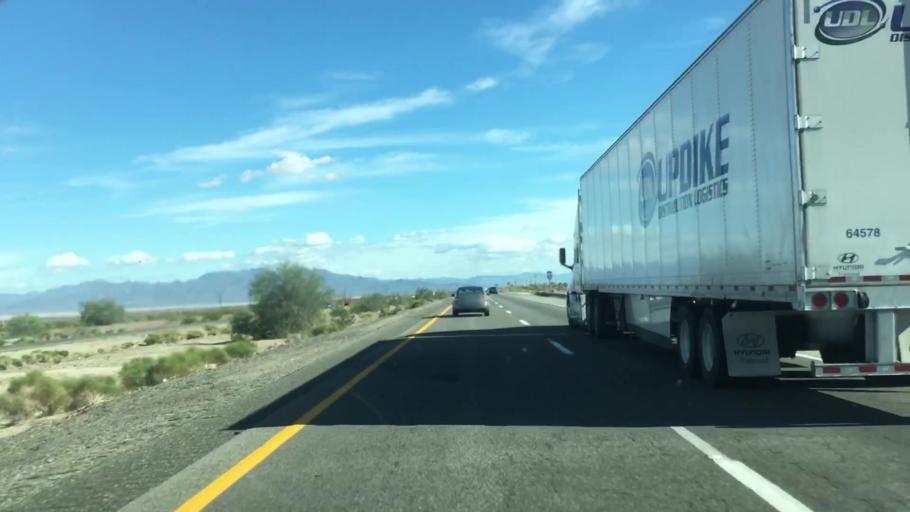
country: US
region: California
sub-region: Imperial County
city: Niland
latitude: 33.7104
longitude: -115.3940
